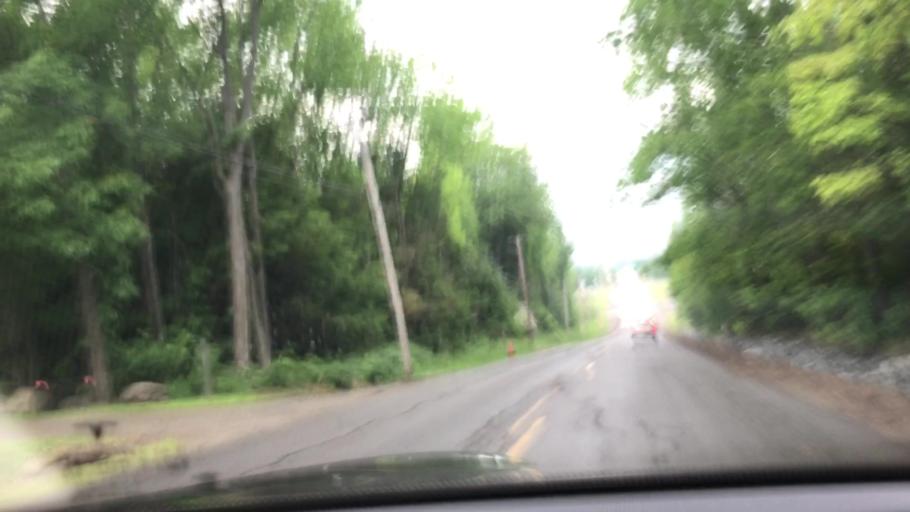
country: US
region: Maine
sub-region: Penobscot County
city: Orono
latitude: 44.8991
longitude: -68.6954
